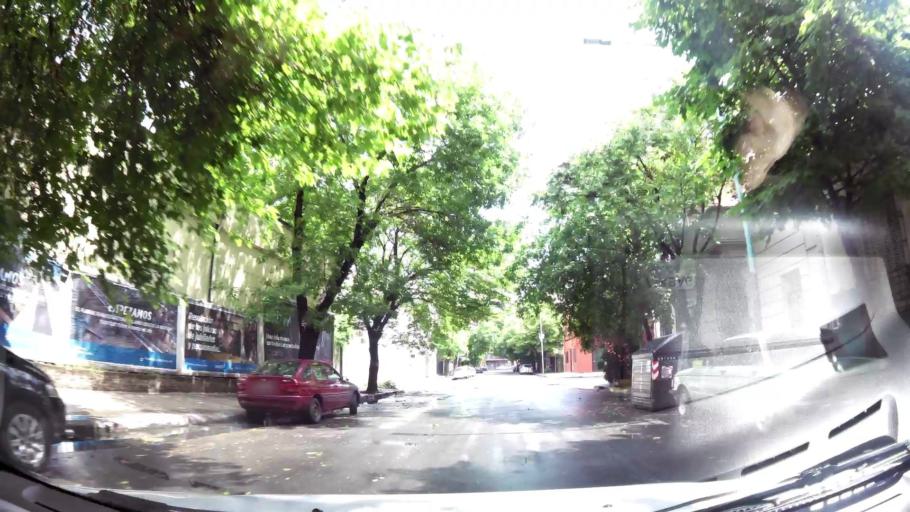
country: AR
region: Buenos Aires F.D.
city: Colegiales
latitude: -34.5909
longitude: -58.4448
